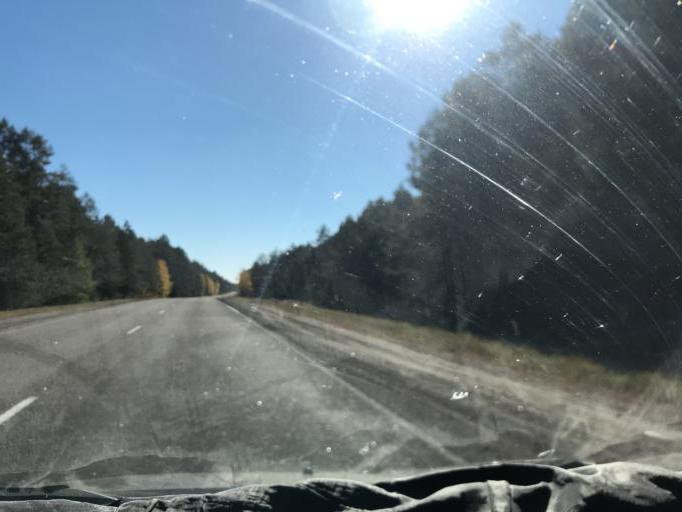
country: BY
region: Gomel
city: Kalinkavichy
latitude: 52.4459
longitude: 29.2764
